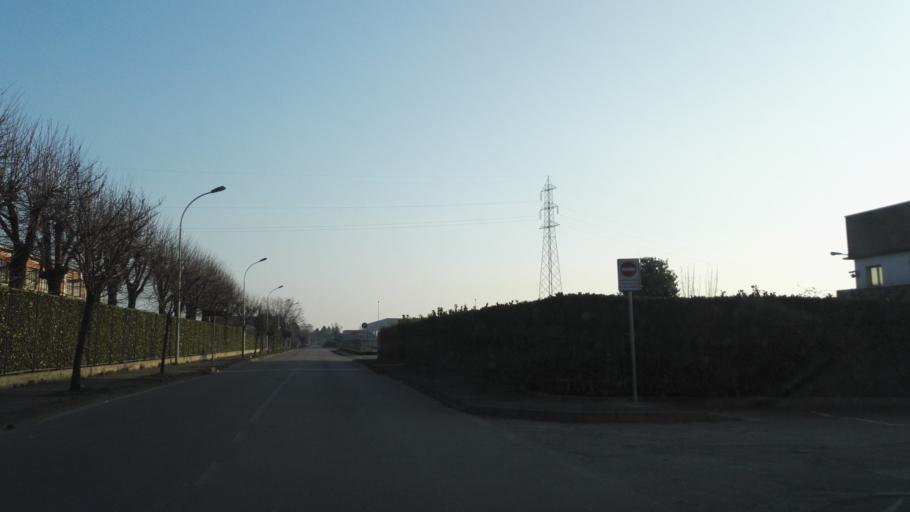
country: IT
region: Lombardy
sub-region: Citta metropolitana di Milano
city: Tribiano
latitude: 45.4119
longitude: 9.3826
